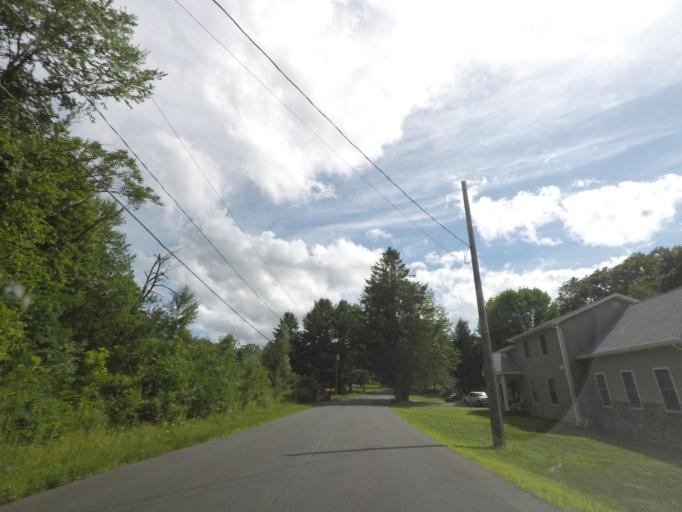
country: US
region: New York
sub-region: Rensselaer County
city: Averill Park
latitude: 42.6572
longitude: -73.5494
